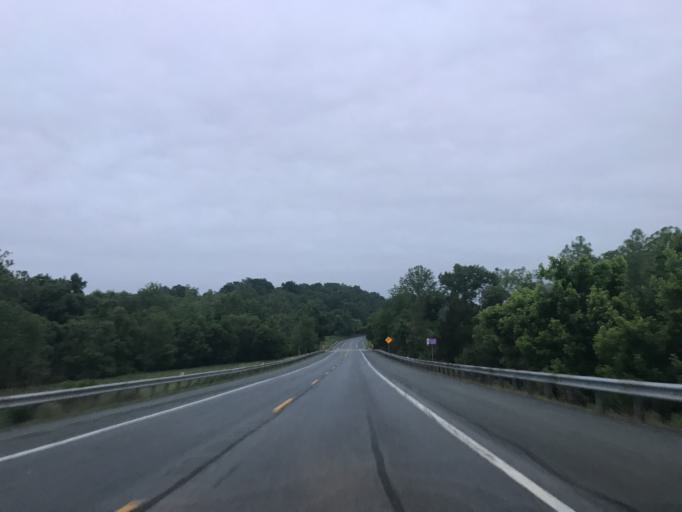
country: US
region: Maryland
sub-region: Frederick County
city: Linganore
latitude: 39.4494
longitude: -77.2482
